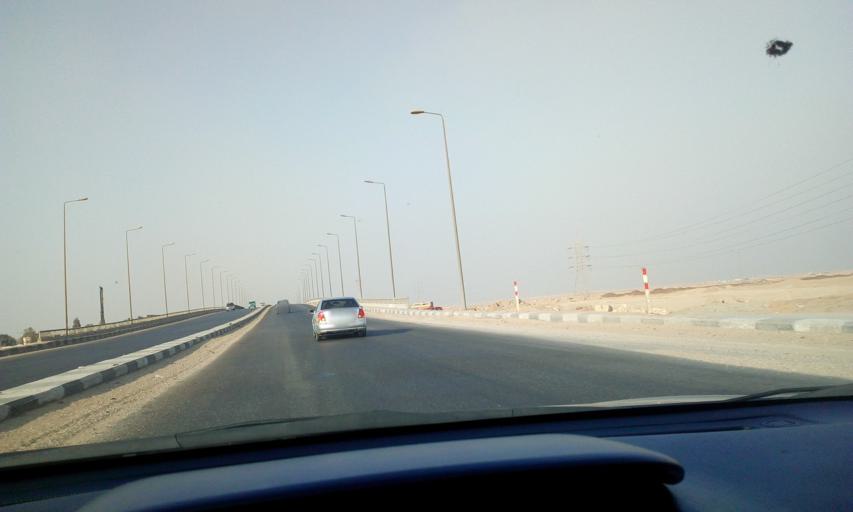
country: EG
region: Al Jizah
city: Madinat Sittah Uktubar
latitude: 29.8726
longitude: 31.0745
